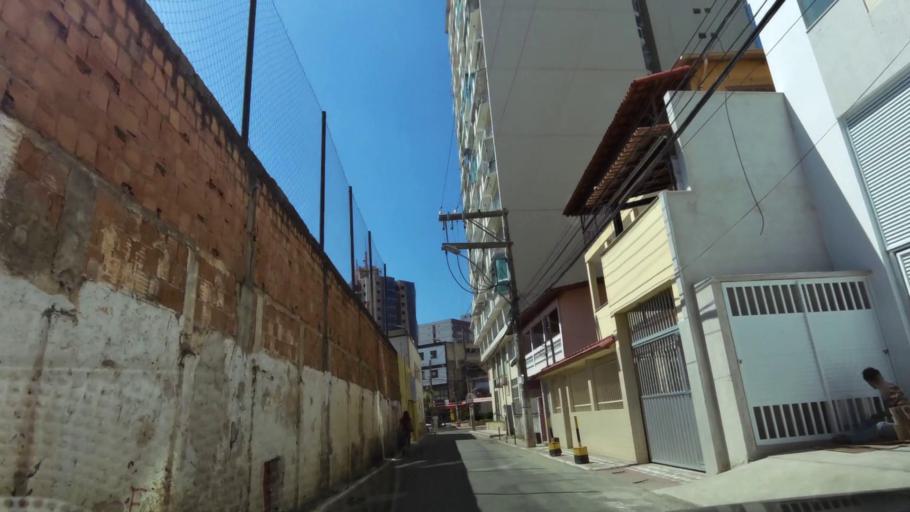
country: BR
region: Espirito Santo
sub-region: Guarapari
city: Guarapari
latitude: -20.6717
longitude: -40.4991
